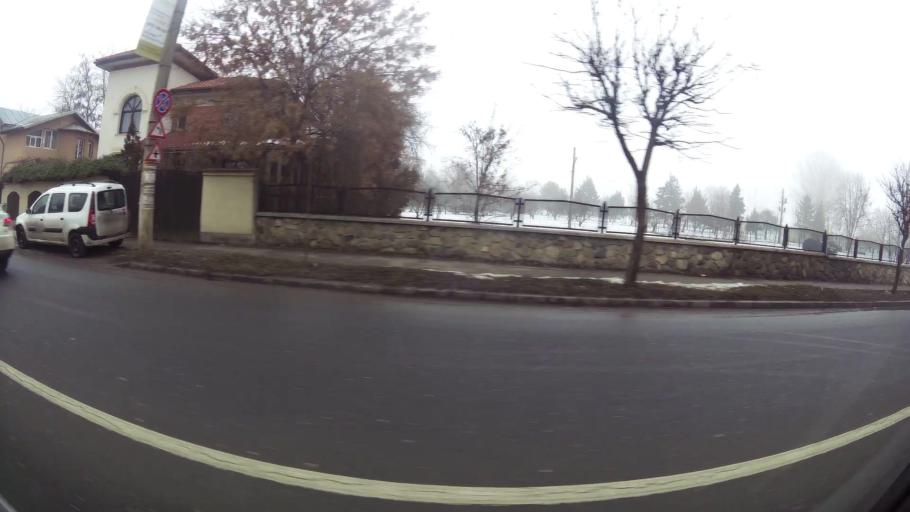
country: RO
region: Ilfov
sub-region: Comuna Chiajna
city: Rosu
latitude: 44.4473
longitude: 26.0155
